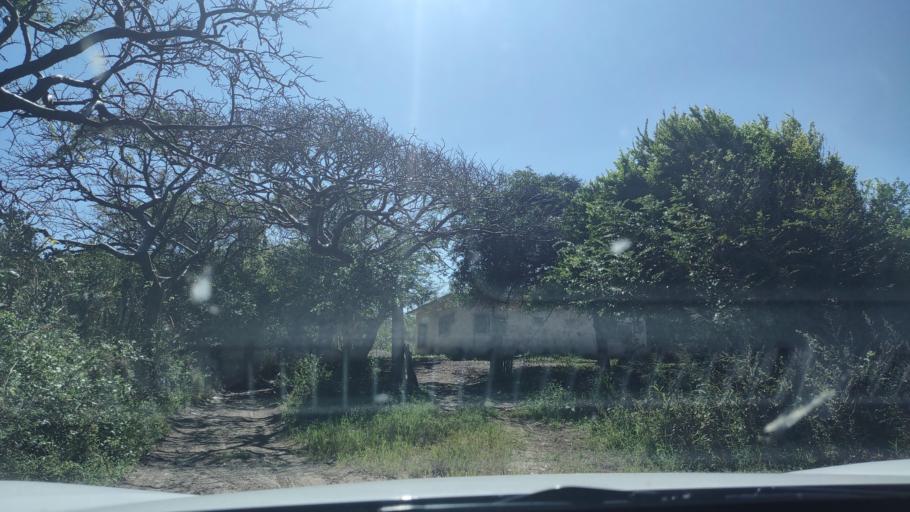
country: MX
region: Veracruz
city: Anton Lizardo
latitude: 19.0519
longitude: -95.9949
